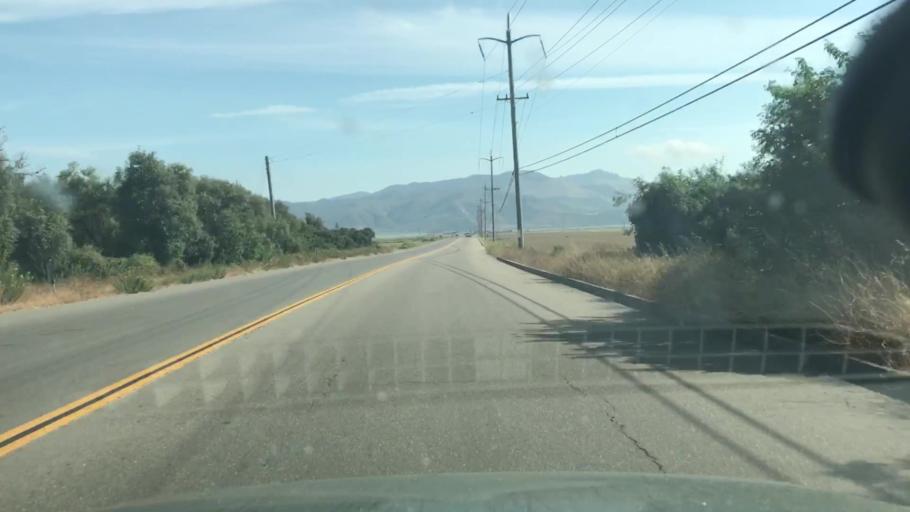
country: US
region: California
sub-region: Santa Barbara County
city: Vandenberg Village
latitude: 34.6705
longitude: -120.4928
